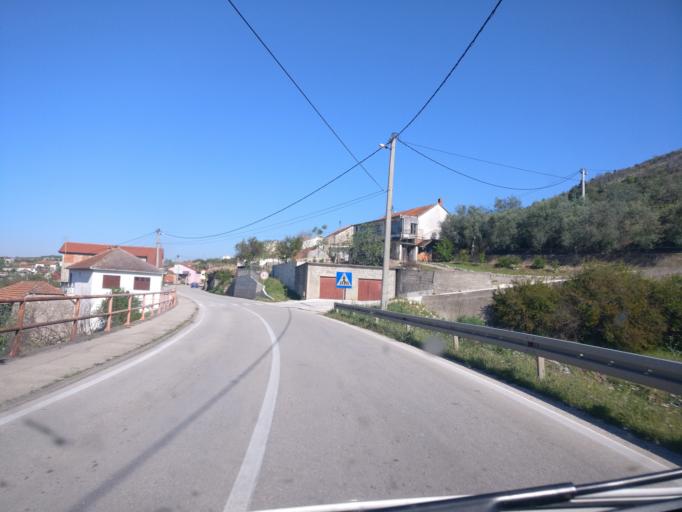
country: BA
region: Federation of Bosnia and Herzegovina
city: Capljina
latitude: 43.1380
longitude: 17.6704
